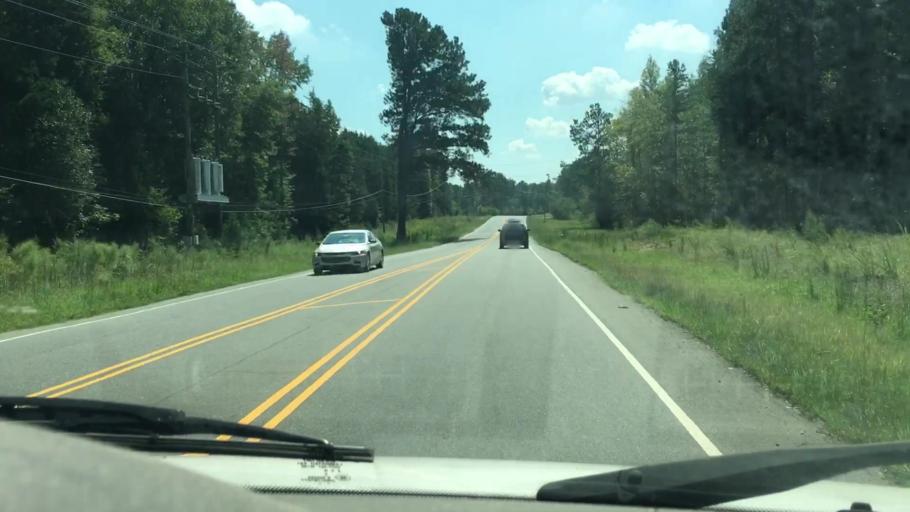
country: US
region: North Carolina
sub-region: Mecklenburg County
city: Huntersville
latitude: 35.3867
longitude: -80.8541
